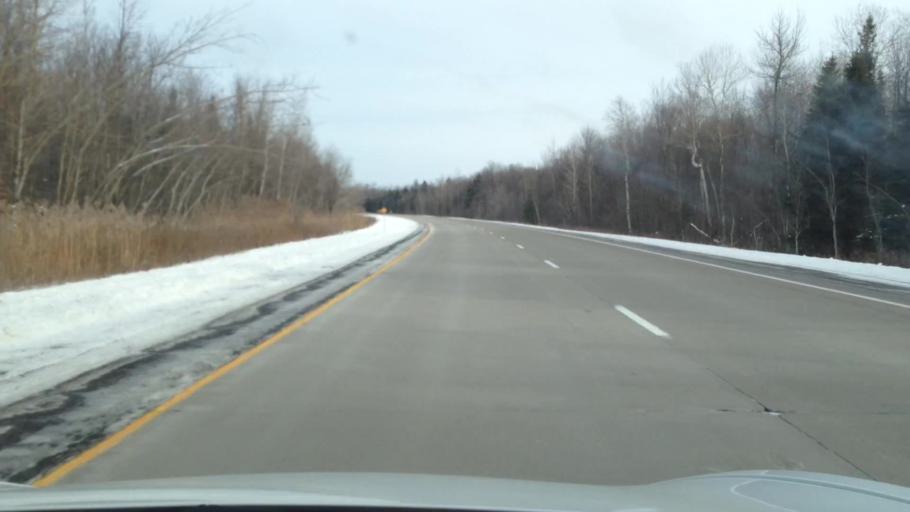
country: CA
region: Ontario
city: Hawkesbury
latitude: 45.5508
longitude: -74.5236
